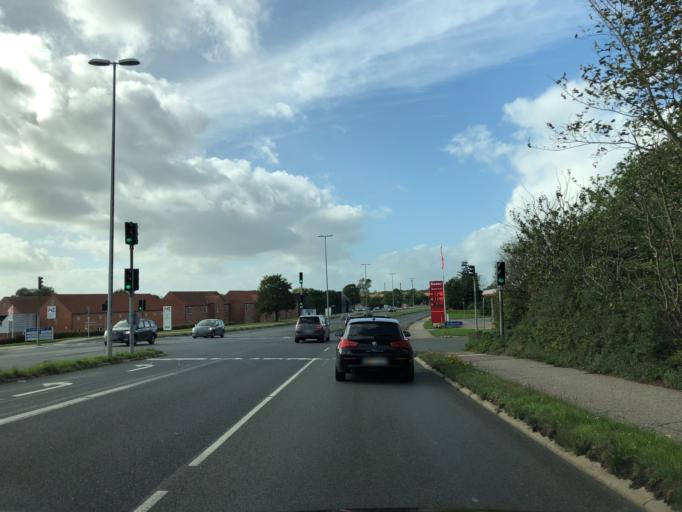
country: DK
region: Central Jutland
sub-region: Holstebro Kommune
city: Holstebro
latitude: 56.3600
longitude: 8.6024
